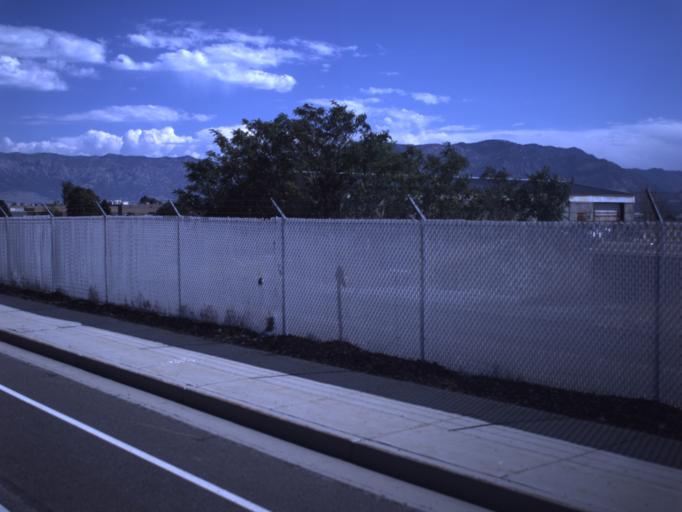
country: US
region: Utah
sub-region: Weber County
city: Riverdale
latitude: 41.1858
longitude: -112.0258
